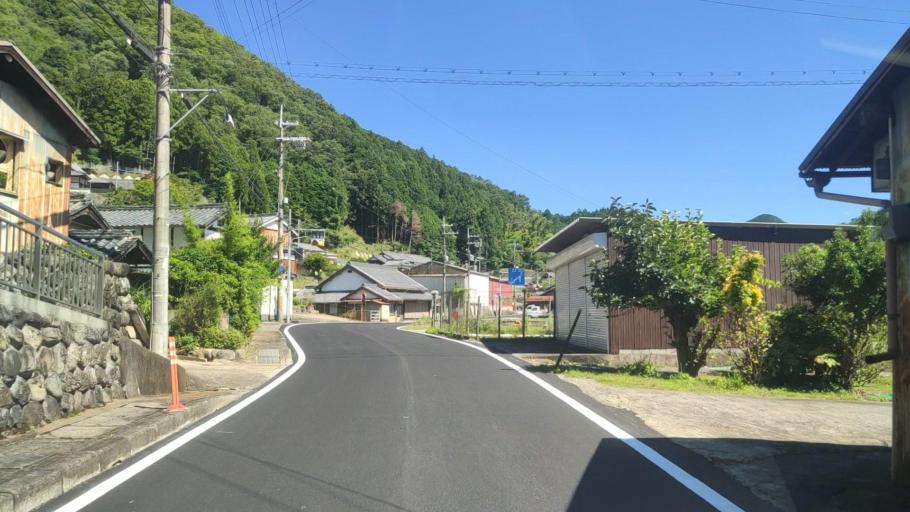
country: JP
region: Nara
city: Yoshino-cho
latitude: 34.3922
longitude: 135.9262
